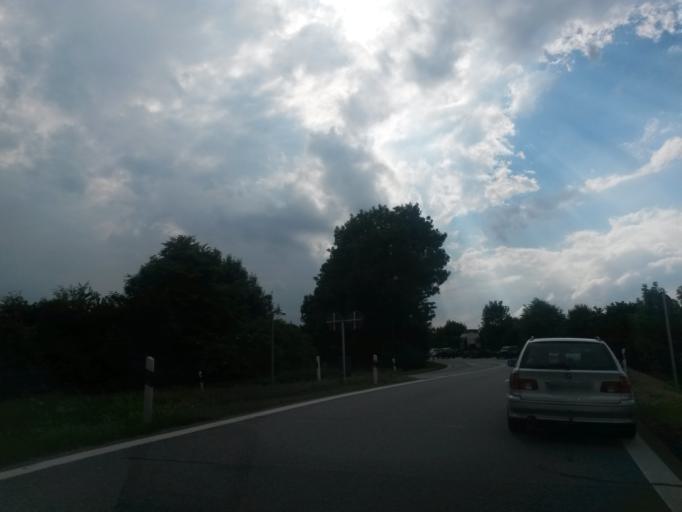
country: DE
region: Bavaria
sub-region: Upper Bavaria
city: Unterschleissheim
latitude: 48.2973
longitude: 11.5801
